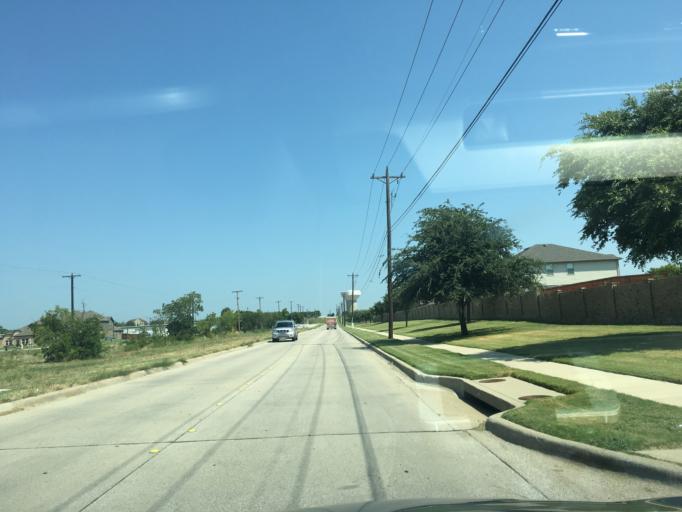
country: US
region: Texas
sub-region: Tarrant County
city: Haslet
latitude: 32.9176
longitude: -97.3314
